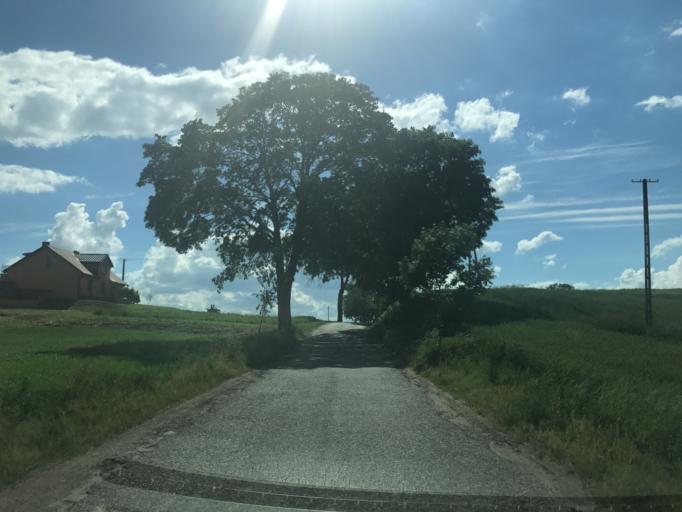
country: PL
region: Kujawsko-Pomorskie
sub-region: Powiat brodnicki
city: Brzozie
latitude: 53.3566
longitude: 19.6137
